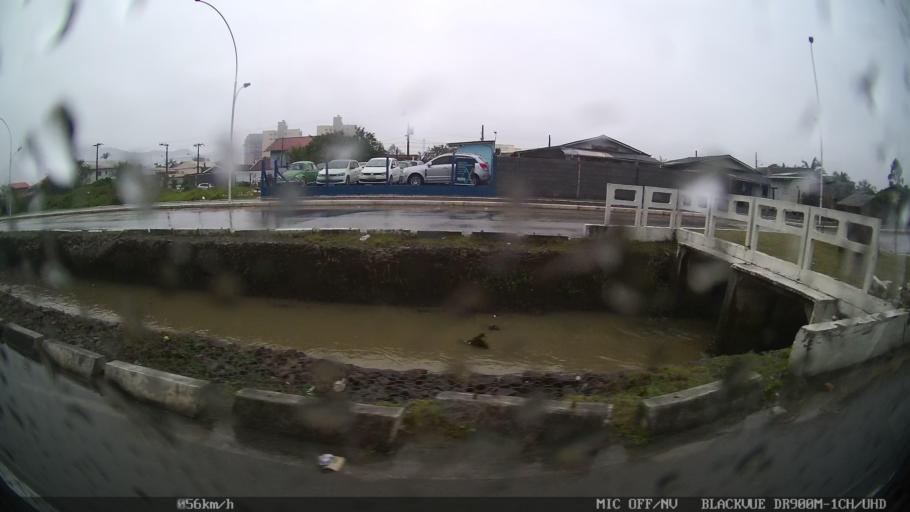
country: BR
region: Santa Catarina
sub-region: Itajai
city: Itajai
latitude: -26.9183
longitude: -48.6871
